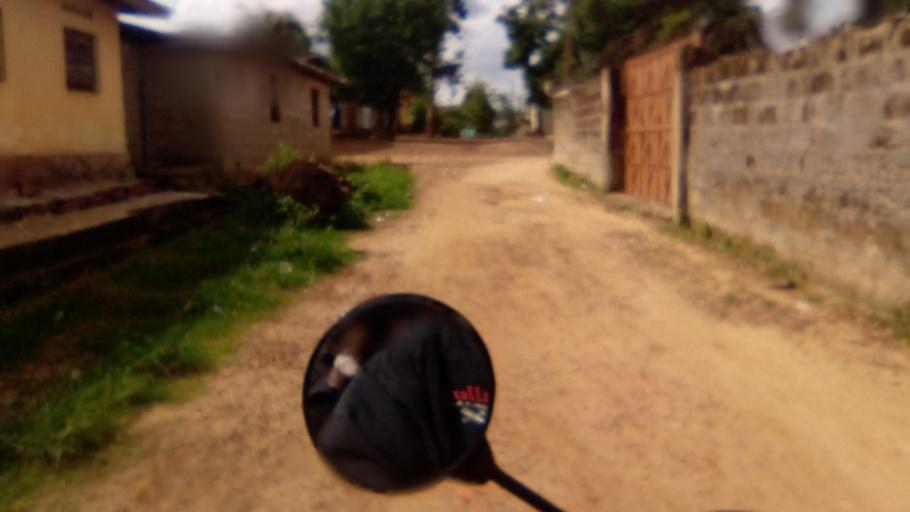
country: SL
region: Southern Province
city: Bo
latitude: 7.9559
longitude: -11.7501
